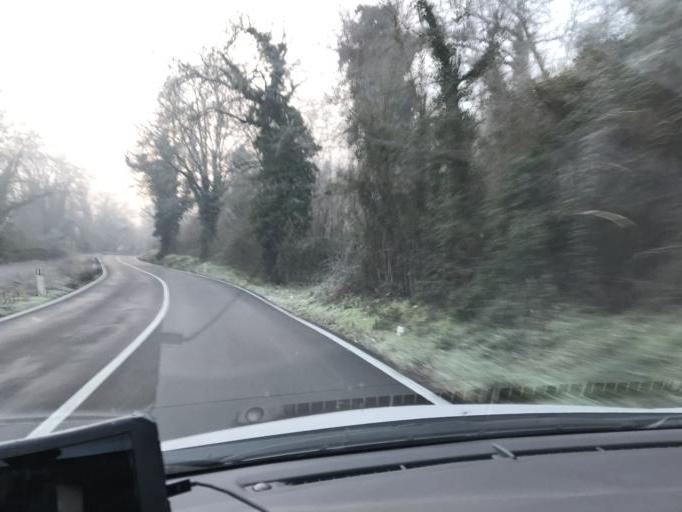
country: IT
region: Latium
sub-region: Provincia di Rieti
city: Colli sul Velino
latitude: 42.5238
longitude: 12.7339
